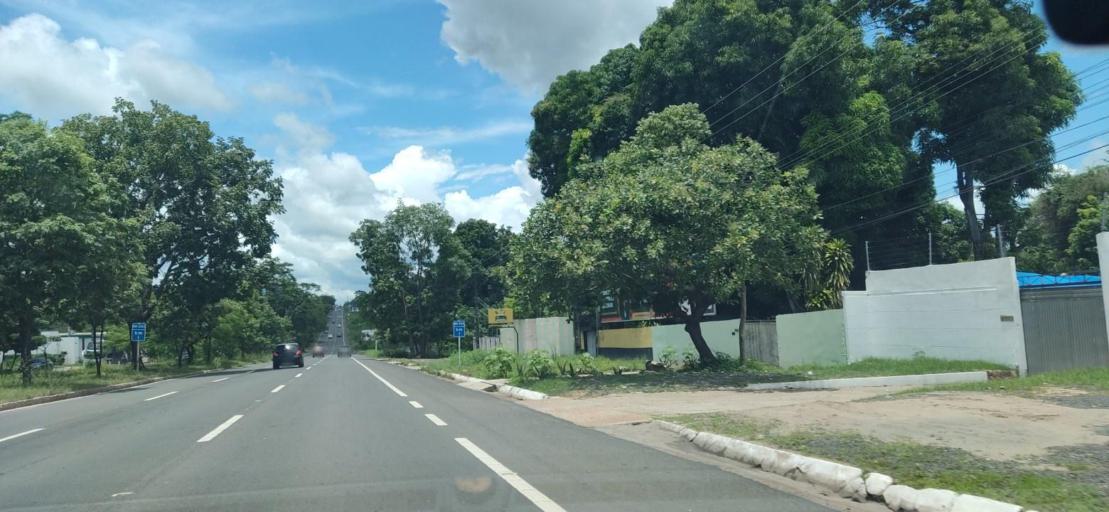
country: BR
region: Piaui
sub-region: Teresina
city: Teresina
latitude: -5.0806
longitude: -42.7587
